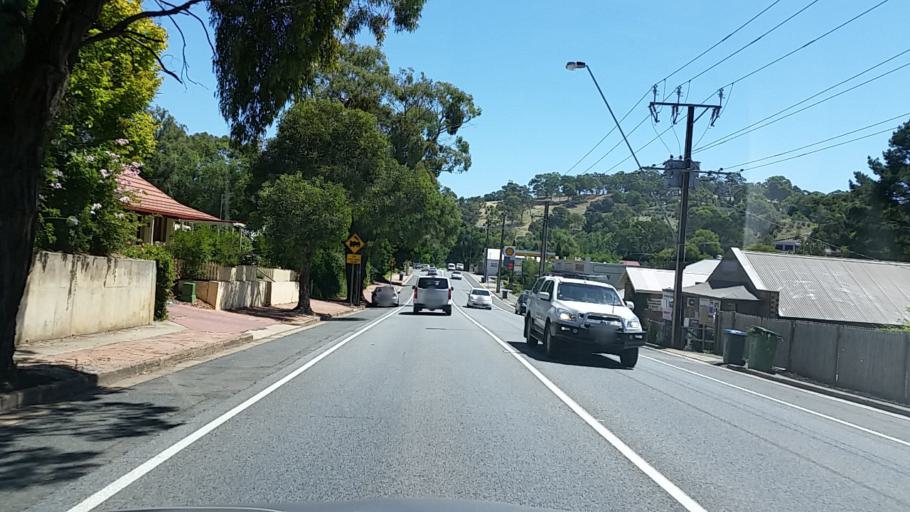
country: AU
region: South Australia
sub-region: Mount Barker
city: Little Hampton
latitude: -35.0492
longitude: 138.8611
